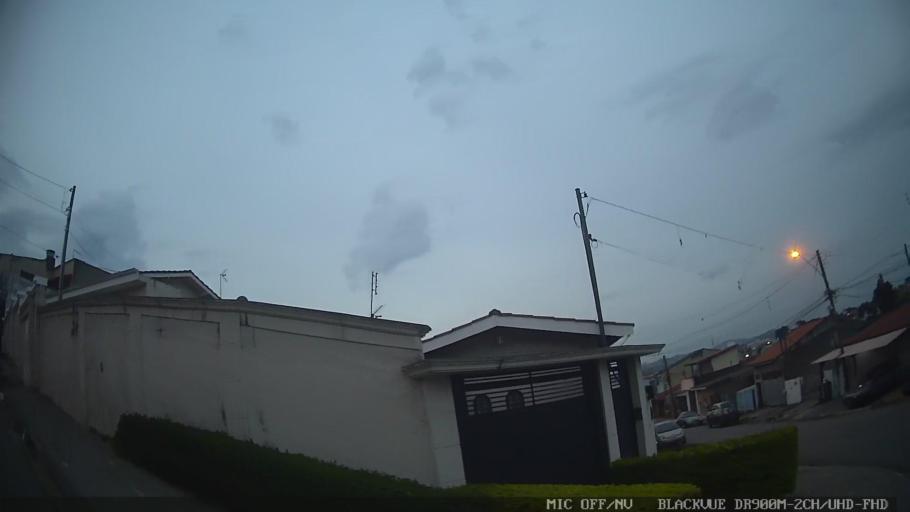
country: BR
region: Sao Paulo
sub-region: Atibaia
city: Atibaia
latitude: -23.1303
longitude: -46.5676
